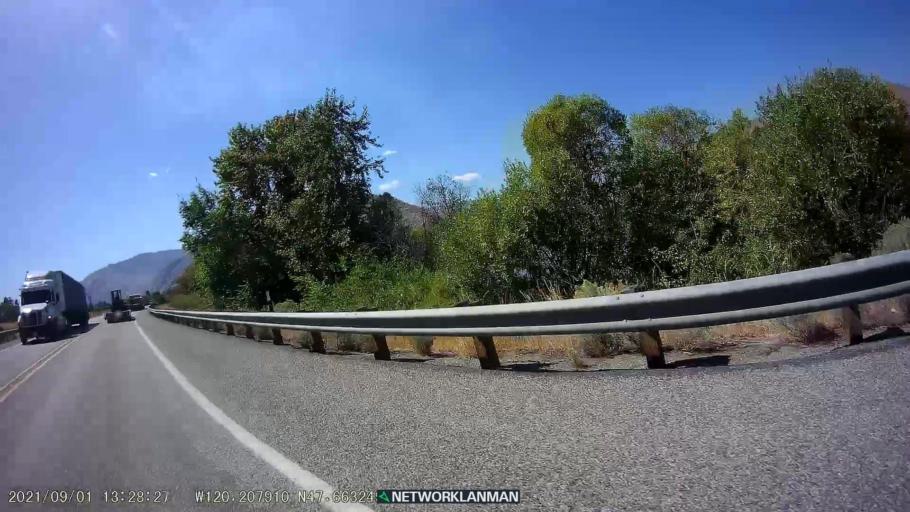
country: US
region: Washington
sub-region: Chelan County
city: Entiat
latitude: 47.6629
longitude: -120.2073
